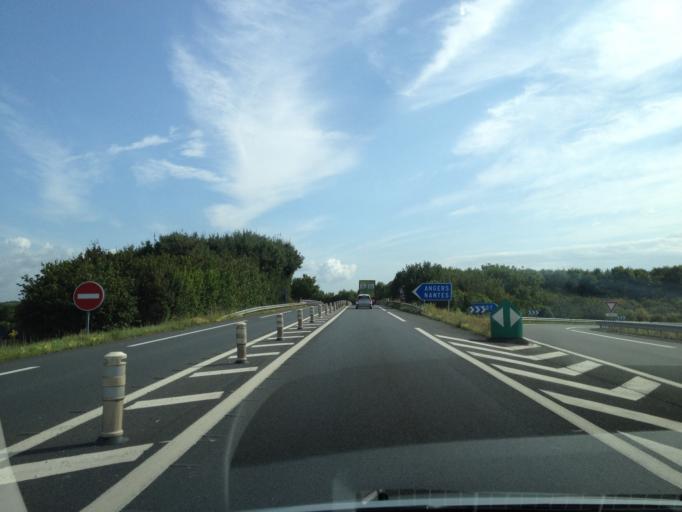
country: FR
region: Pays de la Loire
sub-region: Departement de la Vendee
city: Sainte-Hermine
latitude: 46.5362
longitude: -1.0800
